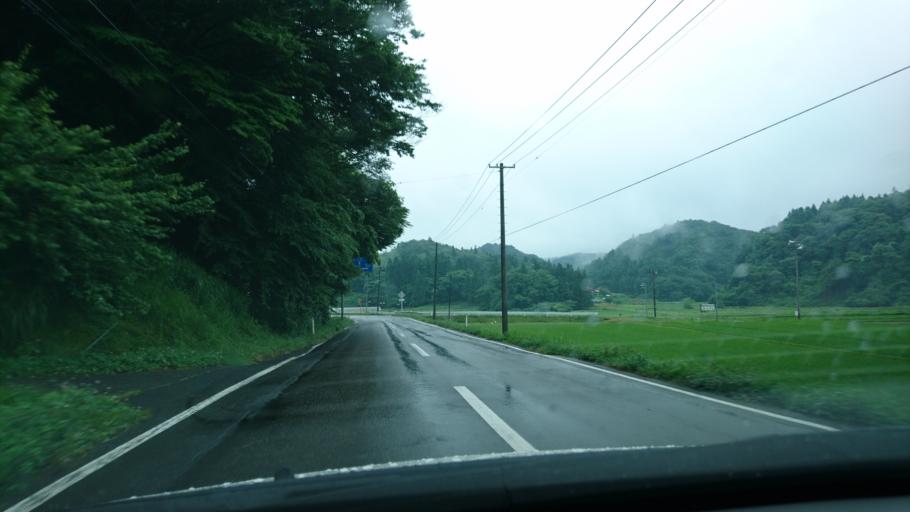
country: JP
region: Iwate
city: Ichinoseki
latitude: 38.8999
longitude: 141.0389
